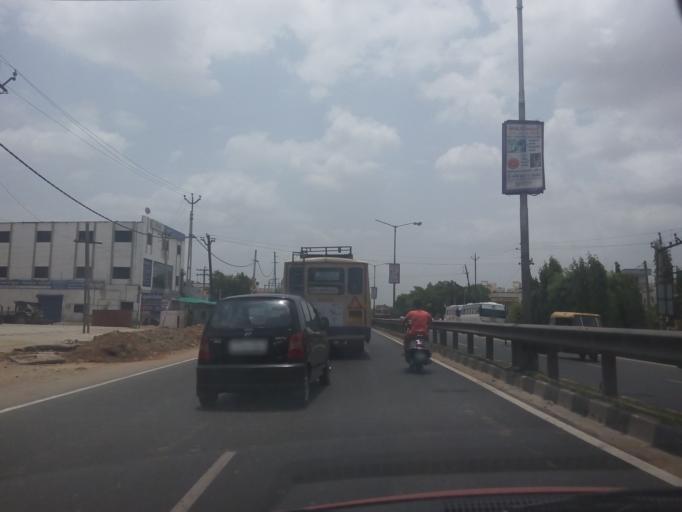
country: IN
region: Gujarat
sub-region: Ahmadabad
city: Sanand
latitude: 22.9872
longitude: 72.3888
